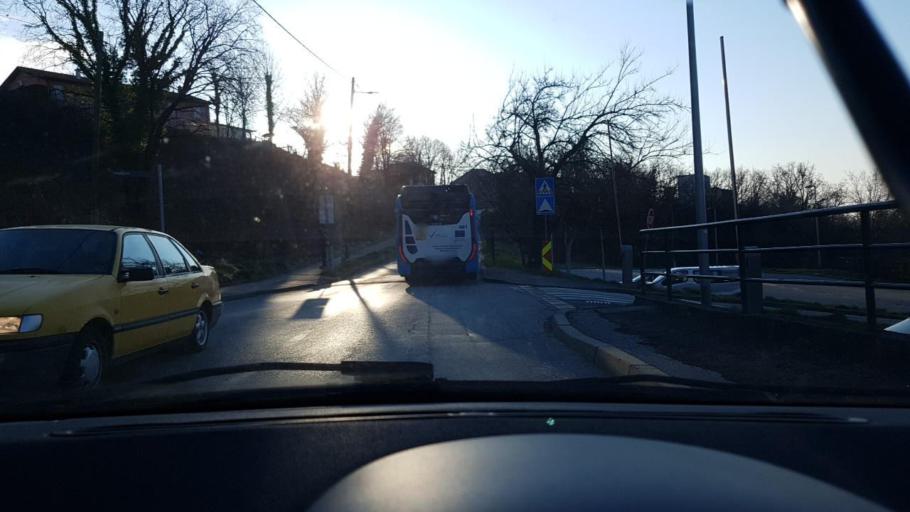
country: HR
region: Grad Zagreb
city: Zagreb
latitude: 45.8515
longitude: 15.9914
